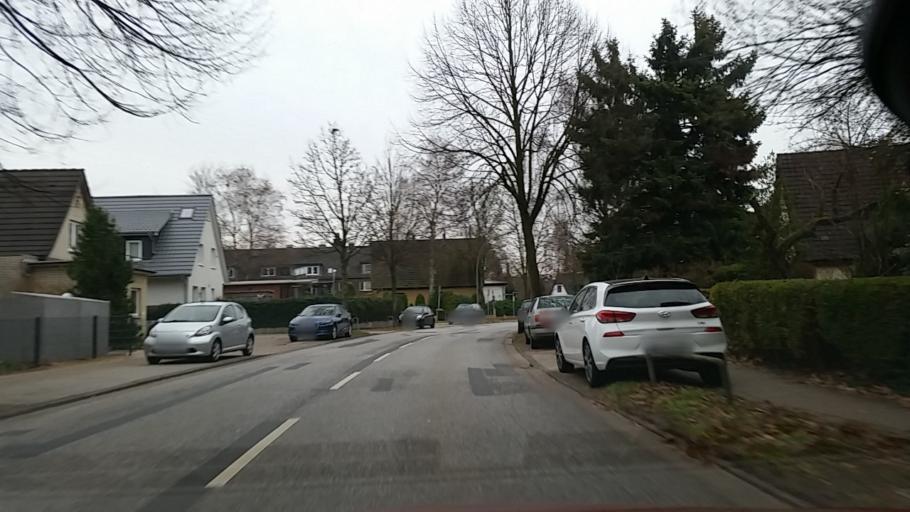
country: DE
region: Hamburg
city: Stellingen
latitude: 53.6294
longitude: 9.9428
